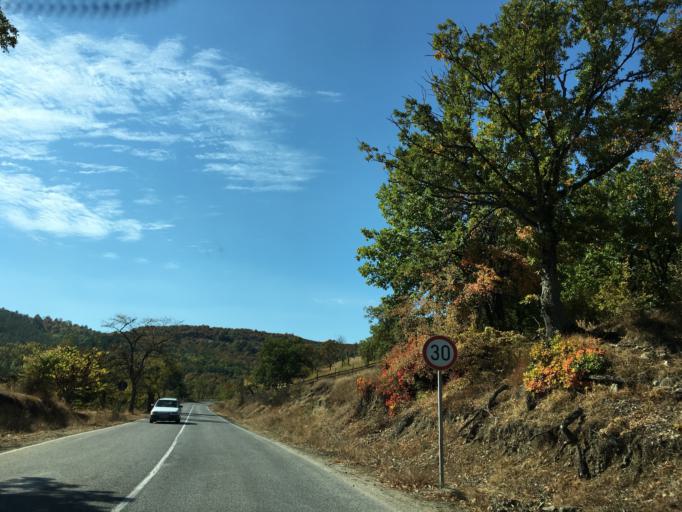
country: BG
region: Kurdzhali
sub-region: Obshtina Krumovgrad
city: Krumovgrad
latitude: 41.4789
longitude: 25.5528
